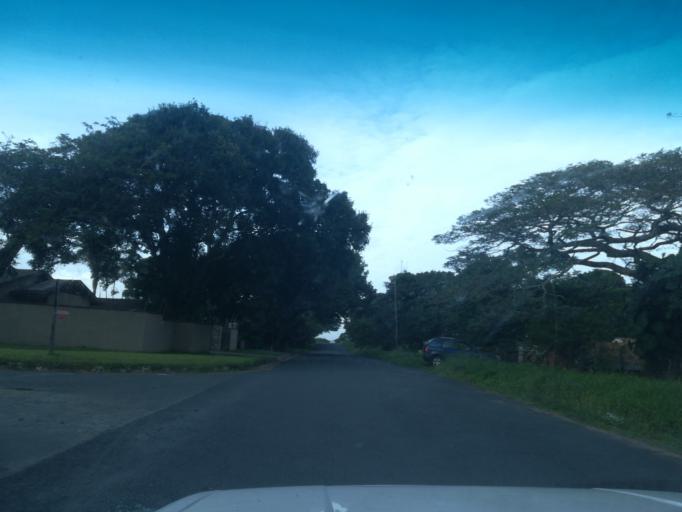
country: ZA
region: KwaZulu-Natal
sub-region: Ugu District Municipality
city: Scottburgh
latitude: -30.2875
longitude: 30.7492
